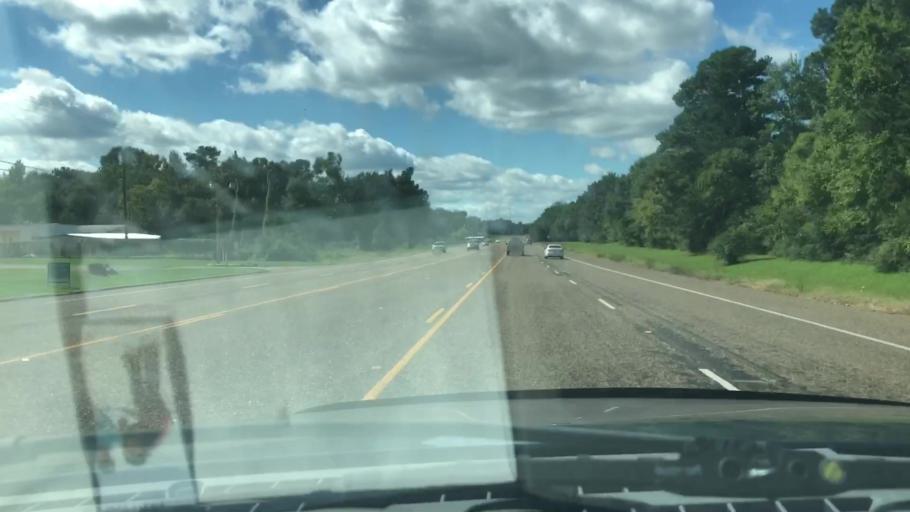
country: US
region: Texas
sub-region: Bowie County
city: Wake Village
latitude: 33.4002
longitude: -94.0826
